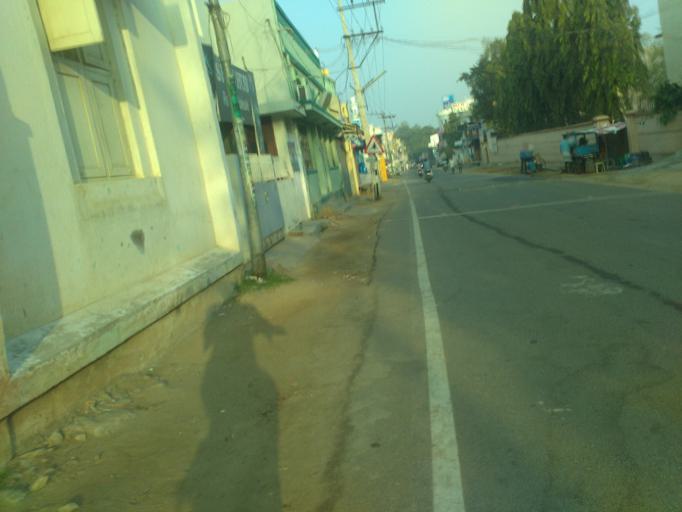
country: IN
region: Tamil Nadu
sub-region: Vellore
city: Ambur
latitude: 12.7851
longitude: 78.7201
